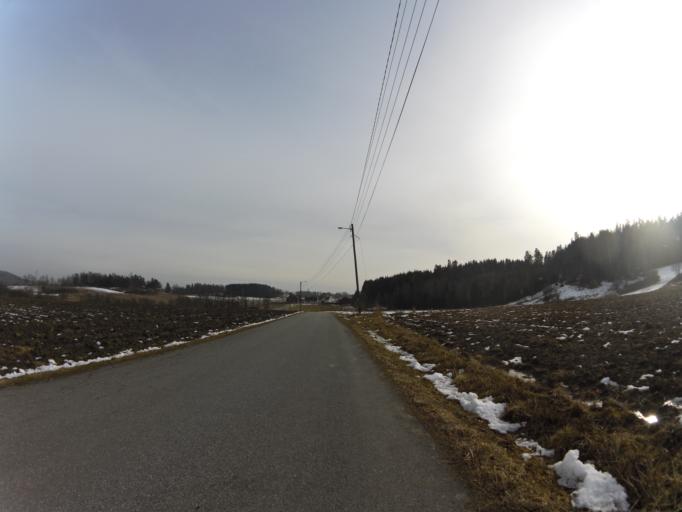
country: NO
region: Ostfold
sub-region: Fredrikstad
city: Fredrikstad
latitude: 59.2769
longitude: 11.0021
